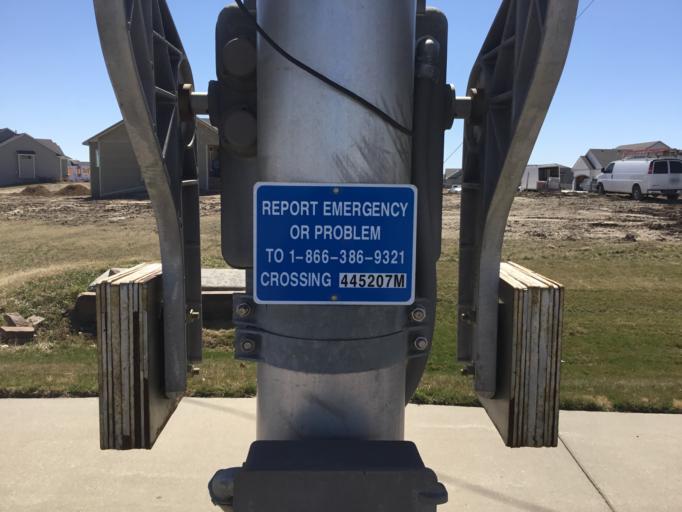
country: US
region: Kansas
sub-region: Sedgwick County
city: Maize
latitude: 37.7520
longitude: -97.4393
